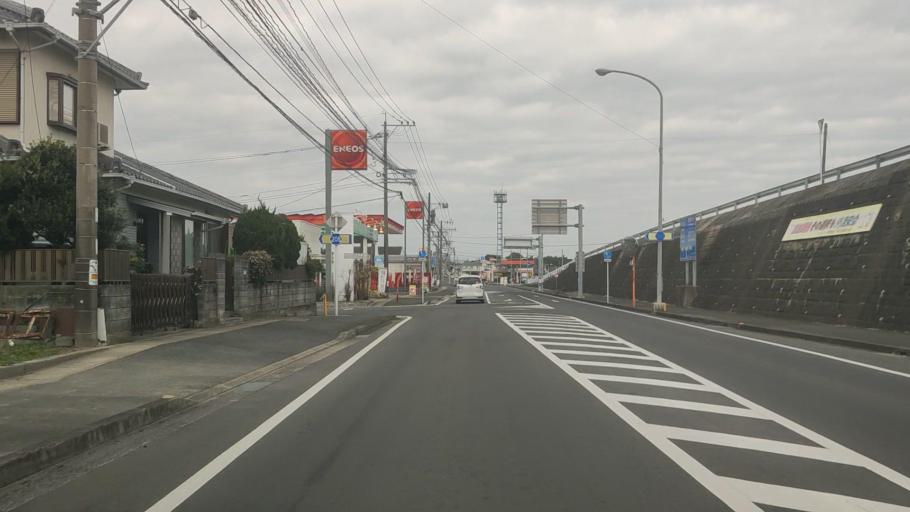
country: JP
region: Nagasaki
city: Shimabara
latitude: 32.8119
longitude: 130.3588
